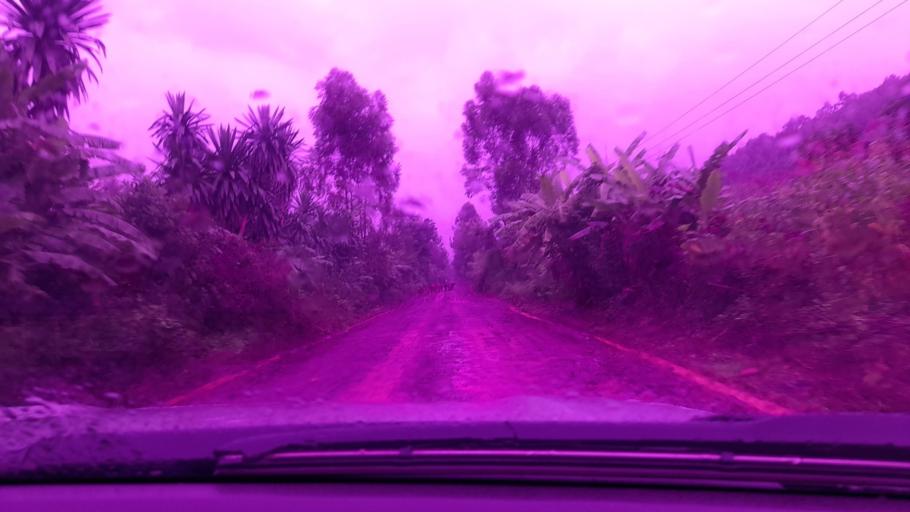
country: ET
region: Oromiya
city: Metu
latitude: 8.3372
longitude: 35.6048
